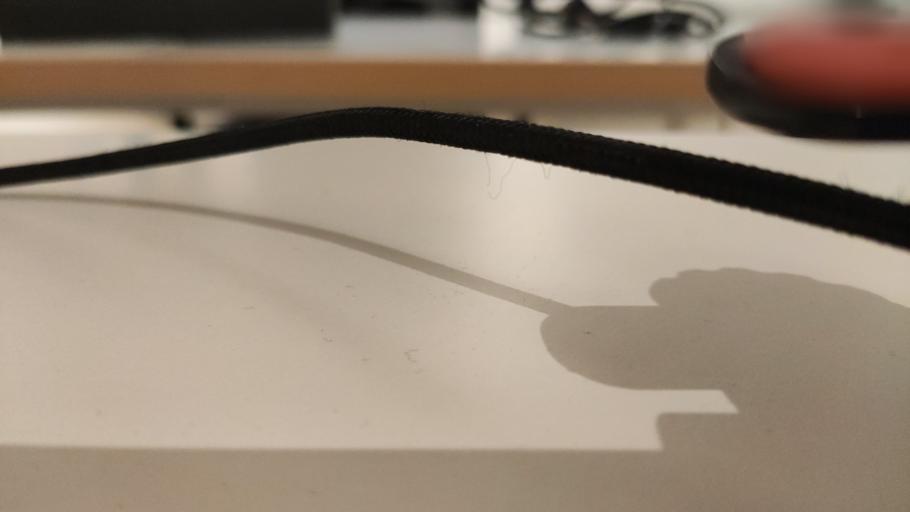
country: RU
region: Moskovskaya
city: Dorokhovo
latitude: 55.4353
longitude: 36.3518
